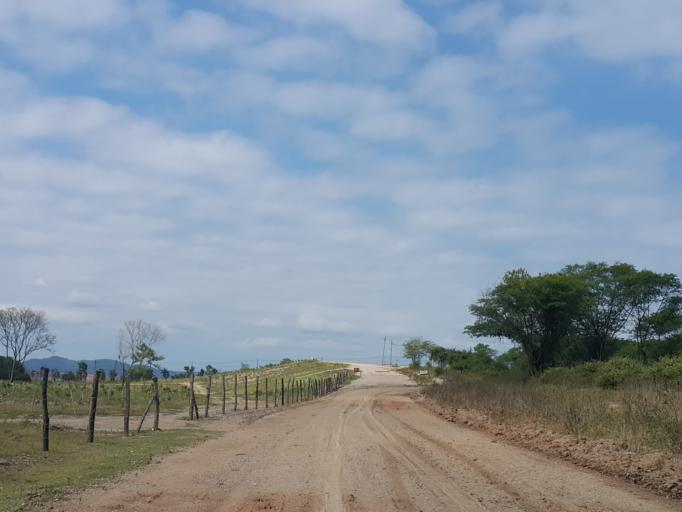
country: TH
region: Lampang
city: Mae Mo
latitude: 18.3334
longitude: 99.7546
